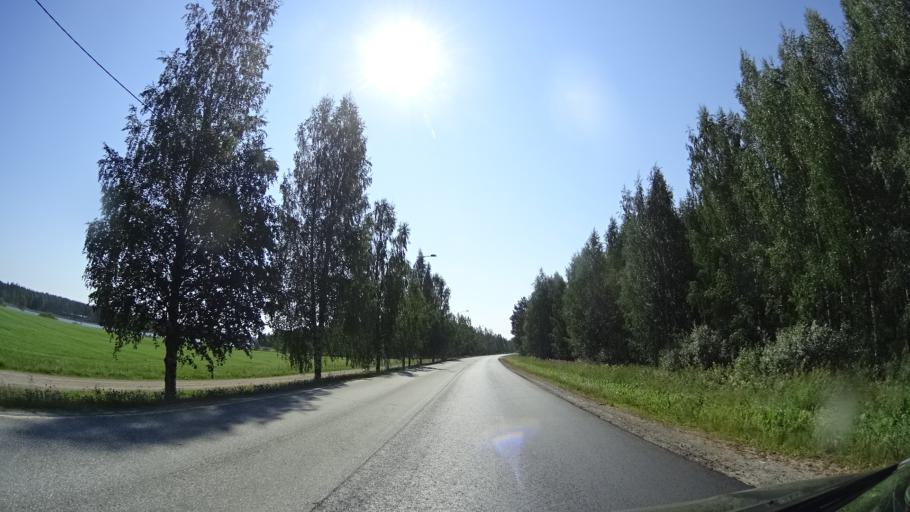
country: FI
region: North Karelia
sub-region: Joensuu
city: Juuka
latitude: 63.2446
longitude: 29.2730
